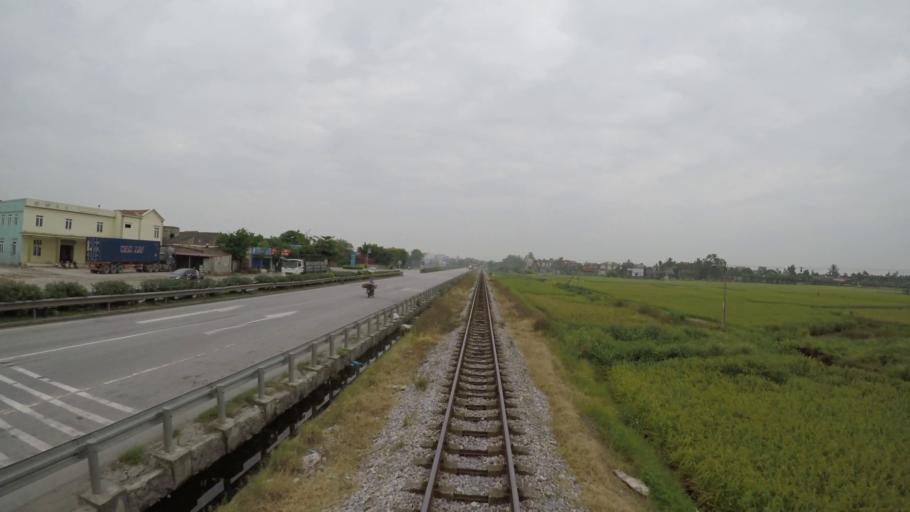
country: VN
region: Hai Duong
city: Phu Thai
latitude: 20.9609
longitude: 106.5207
